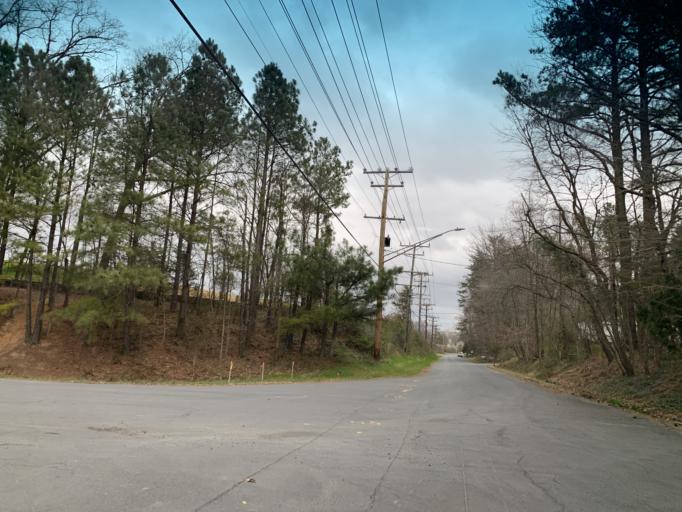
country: US
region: Maryland
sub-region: Harford County
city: Perryman
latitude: 39.4904
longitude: -76.2084
